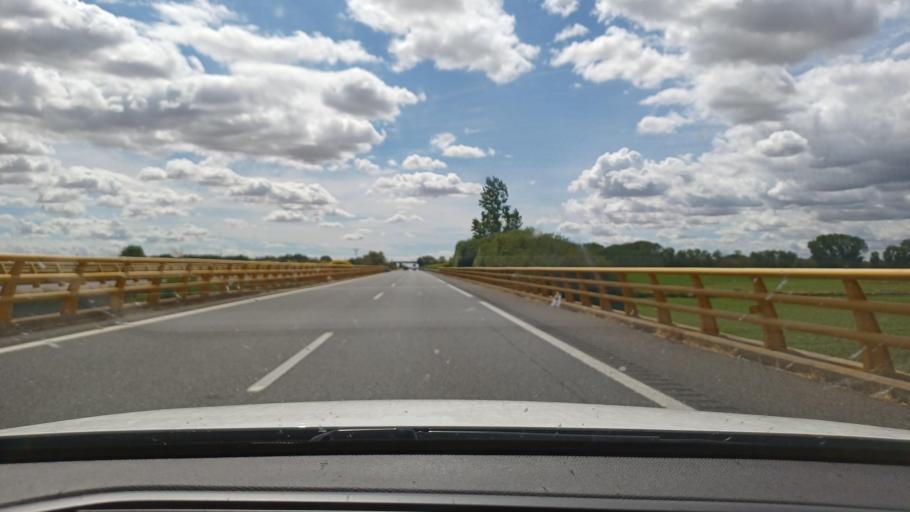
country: ES
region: Castille and Leon
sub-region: Provincia de Palencia
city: Calzada de los Molinos
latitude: 42.3487
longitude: -4.6592
